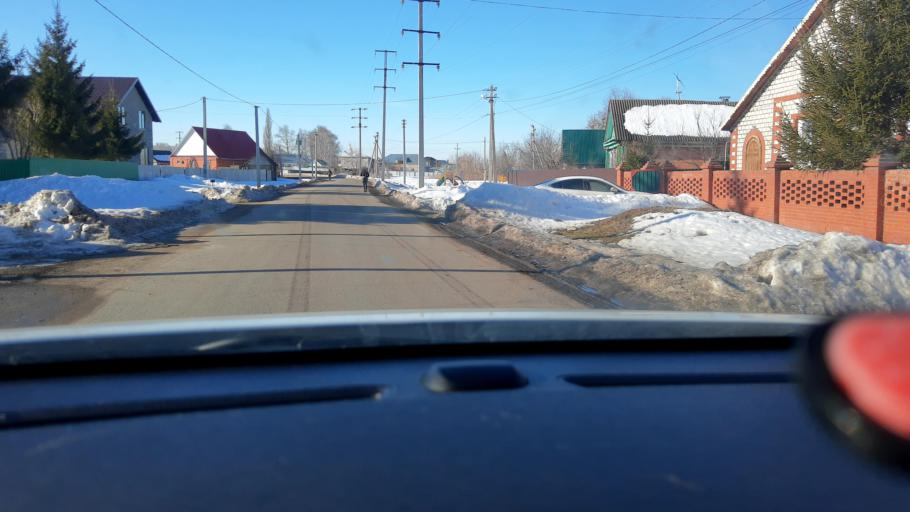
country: RU
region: Bashkortostan
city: Kabakovo
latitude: 54.5203
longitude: 55.9476
